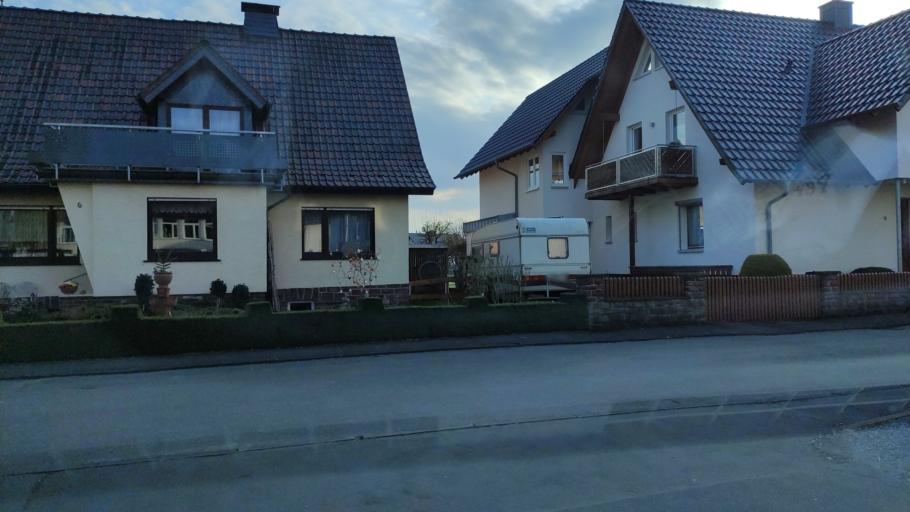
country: DE
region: Lower Saxony
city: Boffzen
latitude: 51.7355
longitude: 9.3599
